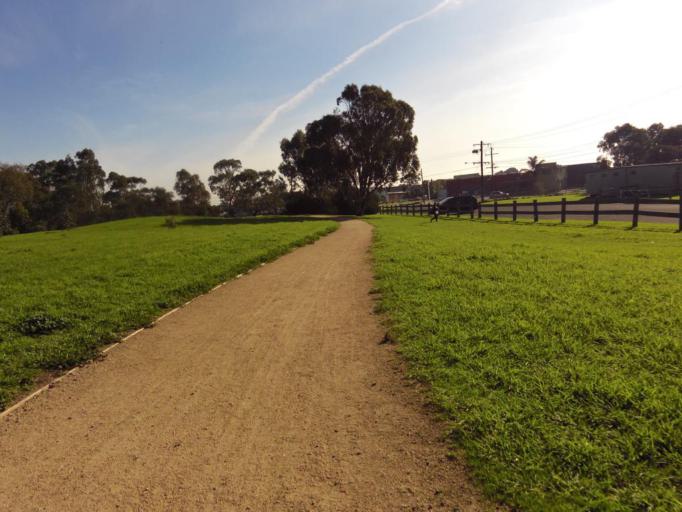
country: AU
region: Victoria
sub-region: Kingston
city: Mordialloc
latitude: -38.0099
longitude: 145.0981
